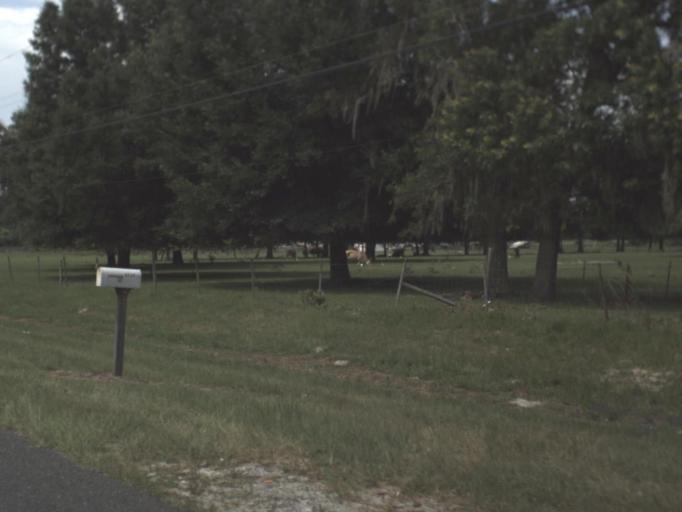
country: US
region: Florida
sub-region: Clay County
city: Green Cove Springs
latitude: 29.8850
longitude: -81.6663
